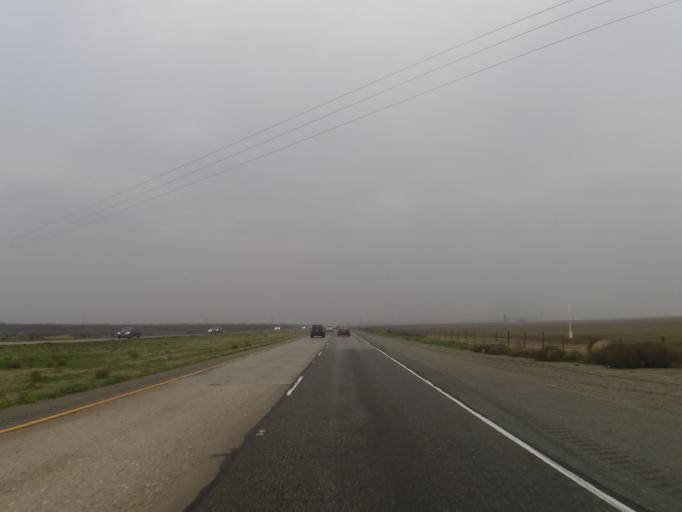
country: US
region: California
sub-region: Kern County
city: Weedpatch
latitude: 35.0764
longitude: -119.0171
